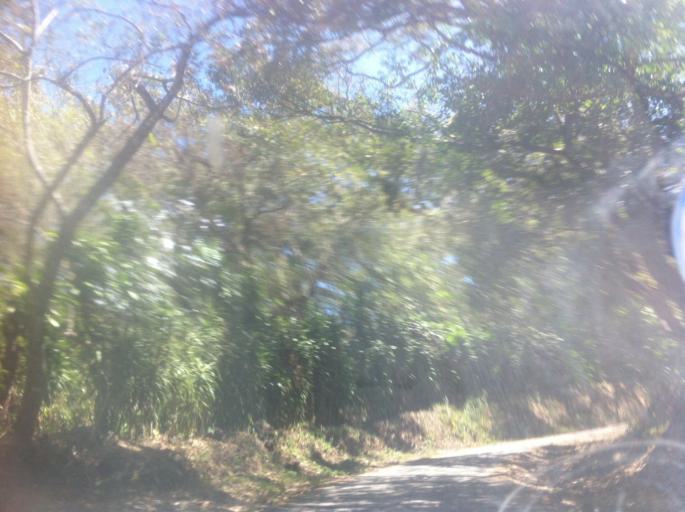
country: NI
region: Granada
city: Diriomo
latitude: 11.8421
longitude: -86.0015
